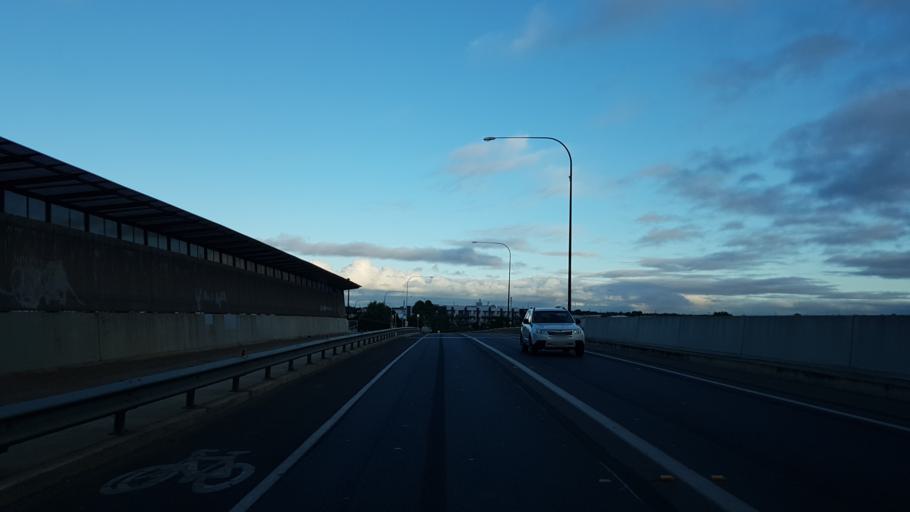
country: AU
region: South Australia
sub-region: Salisbury
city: Ingle Farm
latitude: -34.8037
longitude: 138.6124
